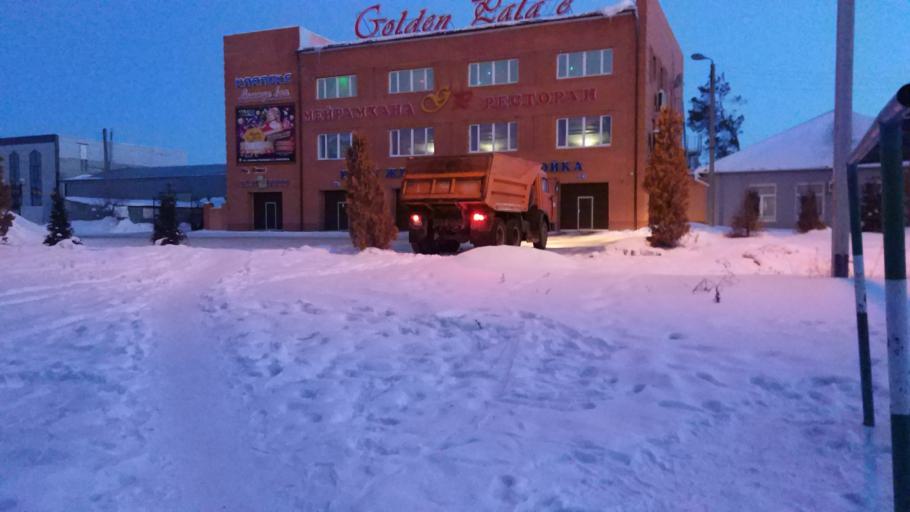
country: KZ
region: Batys Qazaqstan
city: Oral
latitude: 51.2392
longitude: 51.4111
